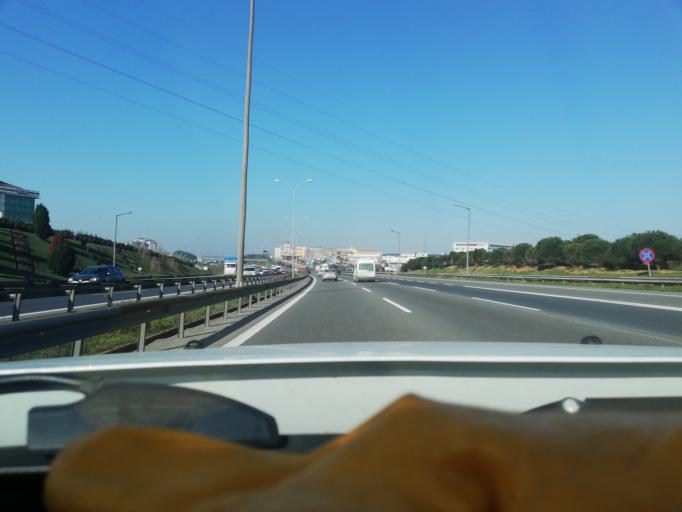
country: TR
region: Istanbul
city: Samandira
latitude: 40.9897
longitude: 29.1911
